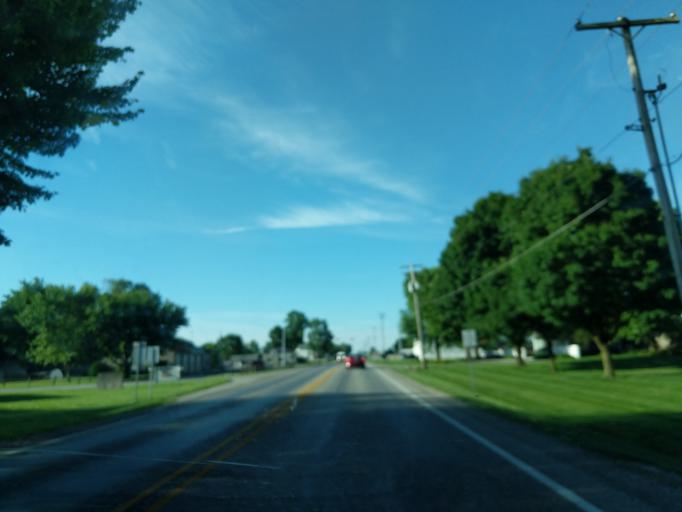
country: US
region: Indiana
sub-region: Madison County
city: Ingalls
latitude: 39.9025
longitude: -85.7707
